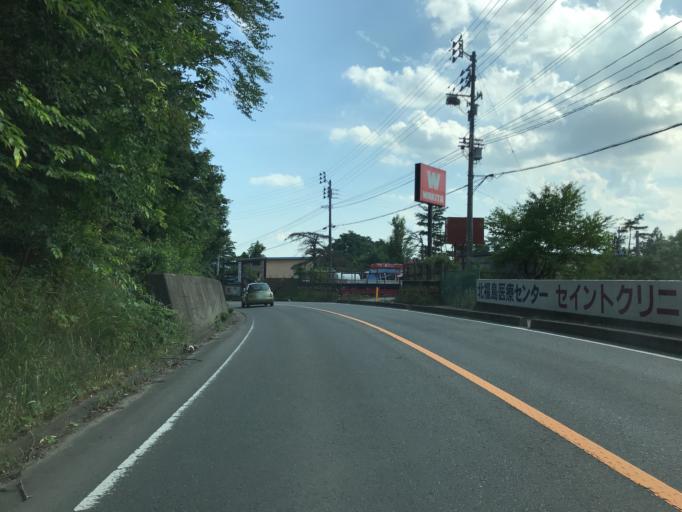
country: JP
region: Fukushima
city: Hobaramachi
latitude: 37.8000
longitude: 140.5172
